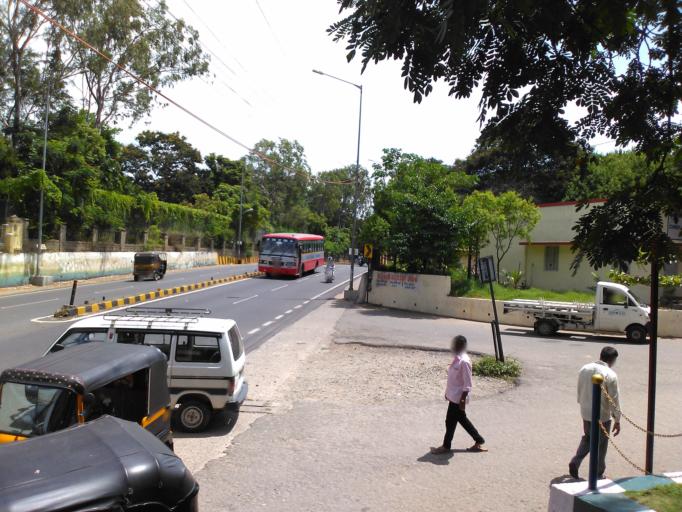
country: IN
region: Karnataka
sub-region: Mysore
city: Mysore
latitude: 12.3163
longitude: 76.6434
